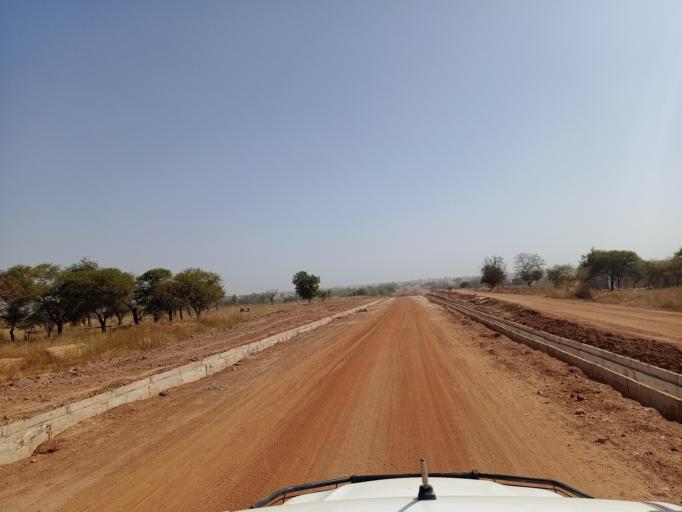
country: BF
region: Centre-Est
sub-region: Province du Boulgou
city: Garango
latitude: 11.5012
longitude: -0.5072
